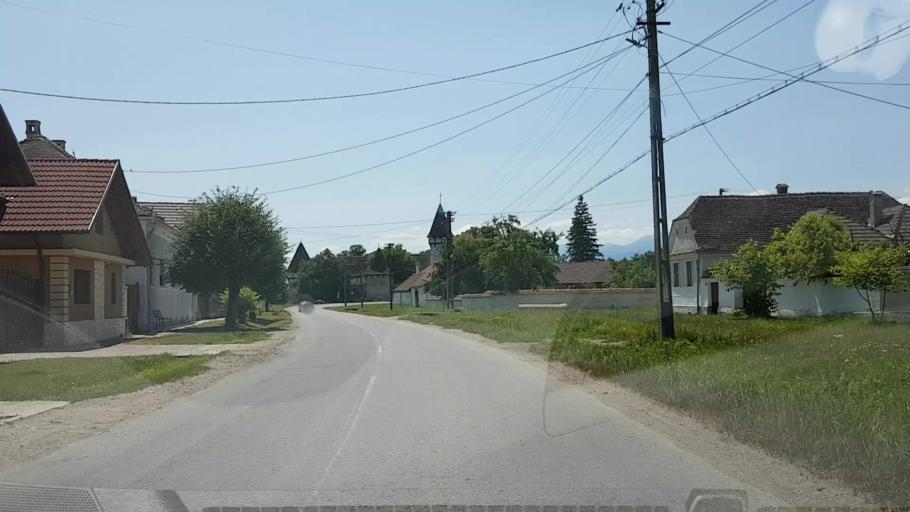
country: RO
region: Brasov
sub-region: Comuna Voila
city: Voila
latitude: 45.8382
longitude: 24.8329
